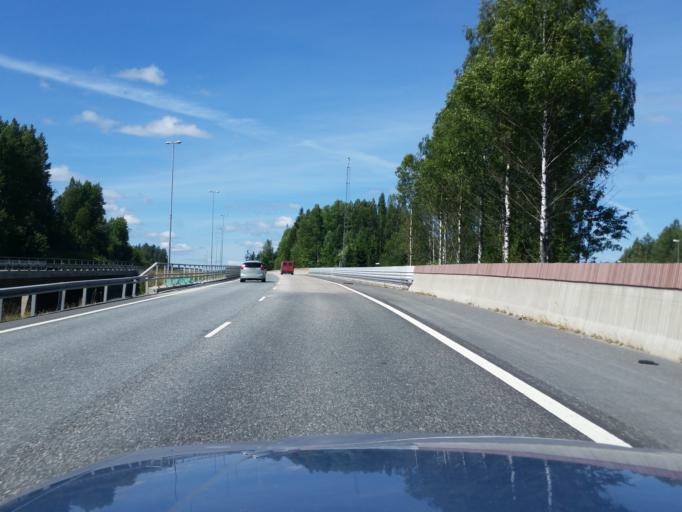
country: FI
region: Uusimaa
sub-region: Helsinki
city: Vihti
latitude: 60.3030
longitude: 24.2729
